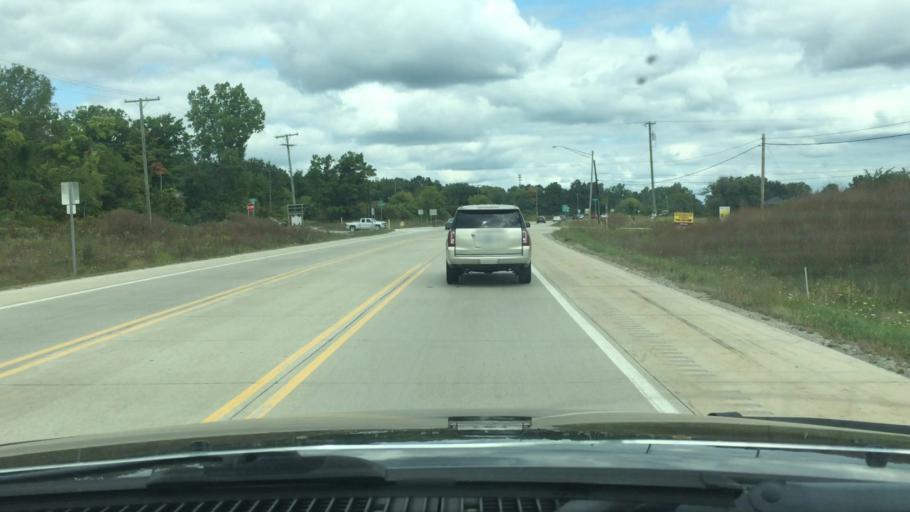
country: US
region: Michigan
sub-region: Lapeer County
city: Almont
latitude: 42.8892
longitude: -83.0425
